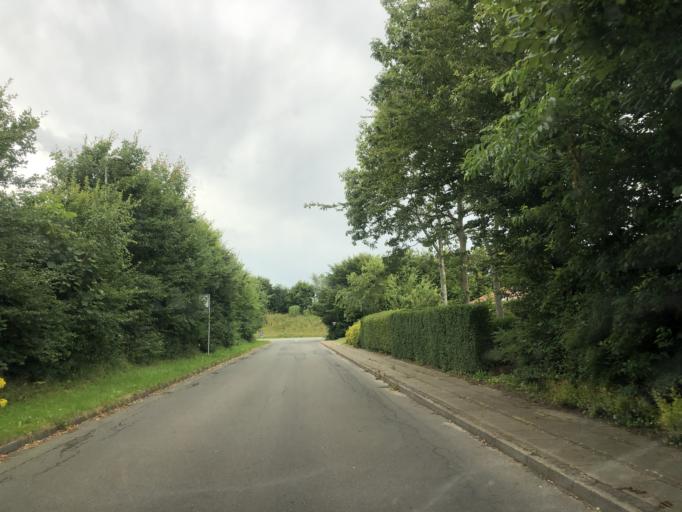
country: DK
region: Central Jutland
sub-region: Holstebro Kommune
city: Holstebro
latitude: 56.3849
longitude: 8.5969
